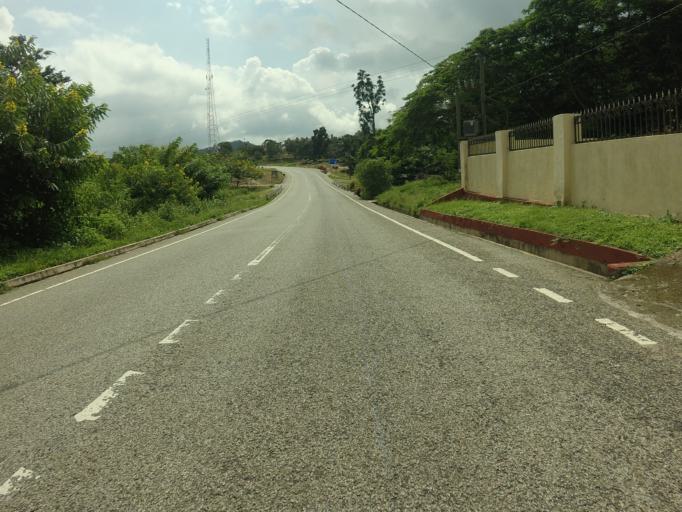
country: GH
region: Volta
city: Kpandu
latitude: 6.8236
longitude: 0.4220
